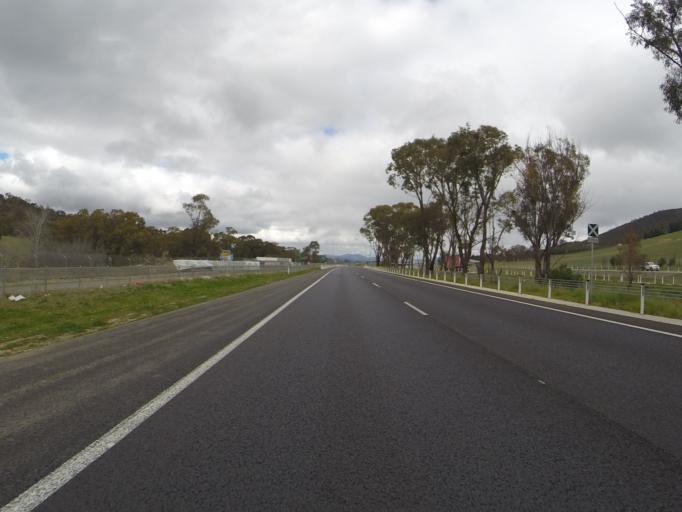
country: AU
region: Australian Capital Territory
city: Canberra
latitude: -35.2258
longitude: 149.1963
